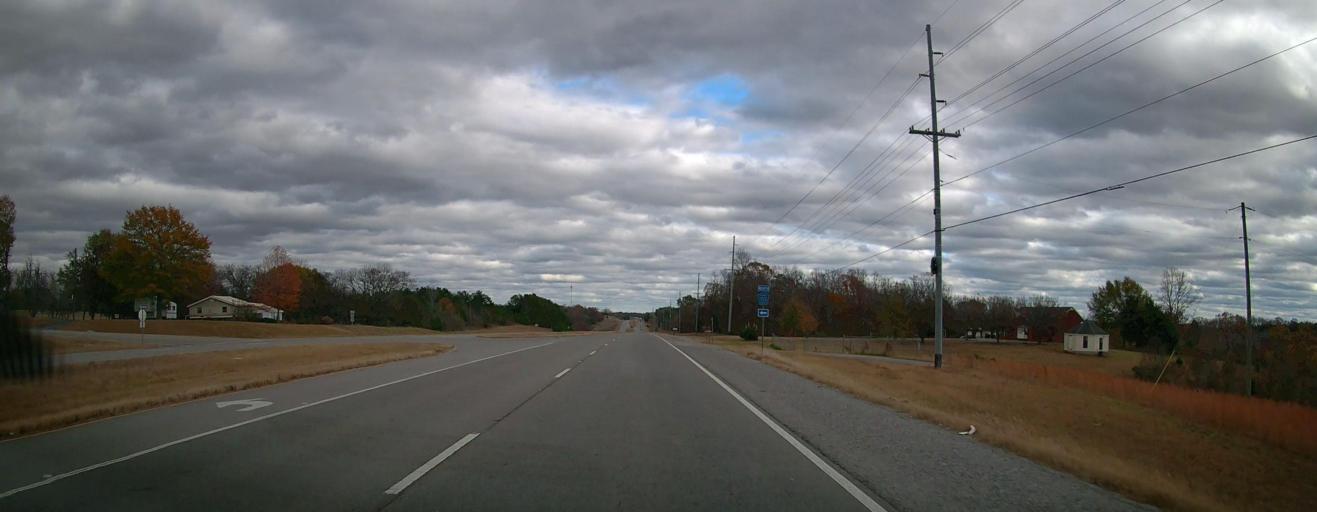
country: US
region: Alabama
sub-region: Lawrence County
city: Moulton
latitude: 34.5625
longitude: -87.3539
